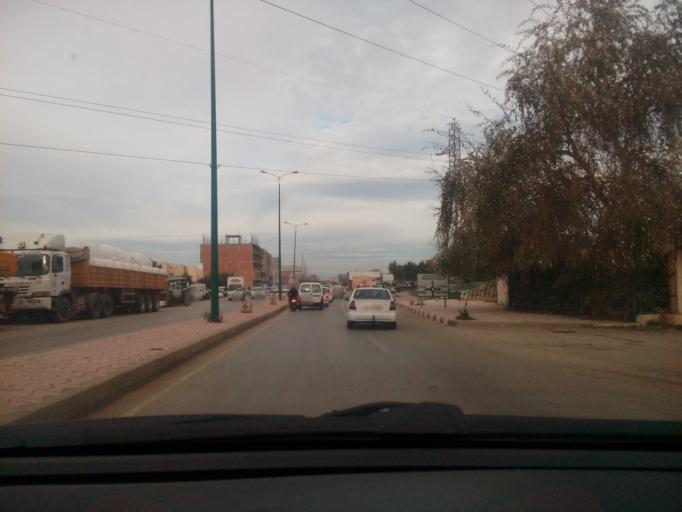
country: DZ
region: Tlemcen
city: Mansoura
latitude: 34.8840
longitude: -1.3514
